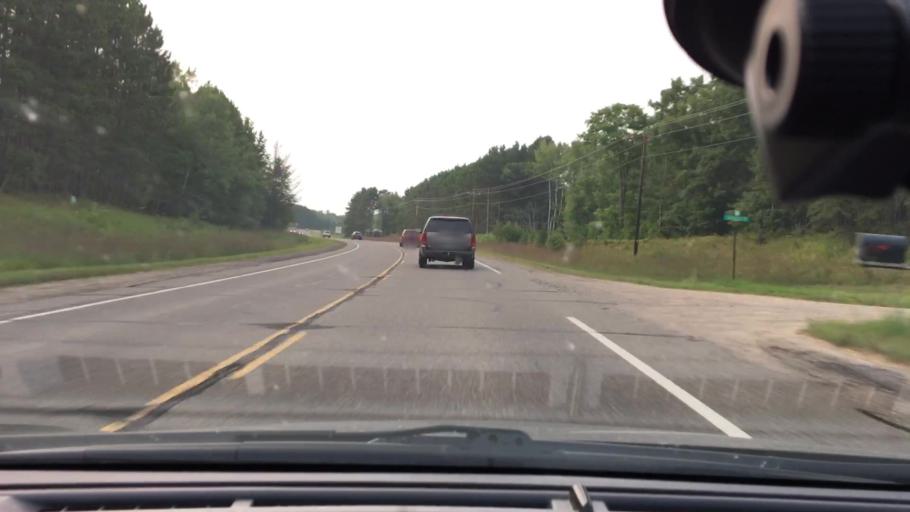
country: US
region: Minnesota
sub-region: Crow Wing County
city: Crosby
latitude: 46.4544
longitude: -93.8801
